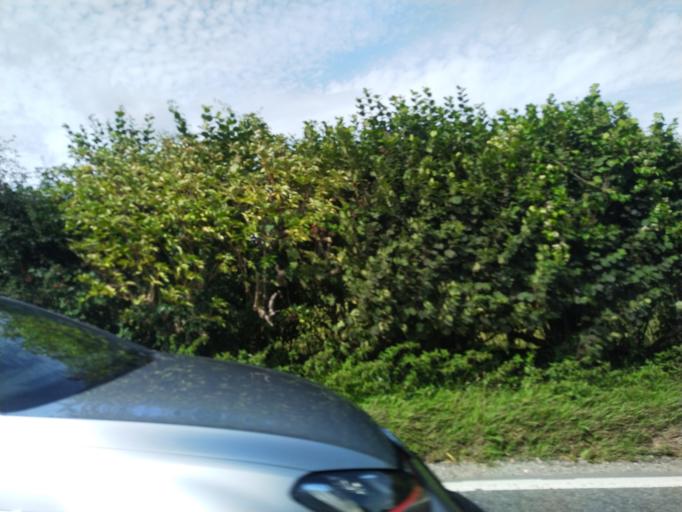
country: GB
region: England
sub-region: Dorset
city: Blandford Forum
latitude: 50.9039
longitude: -2.1937
